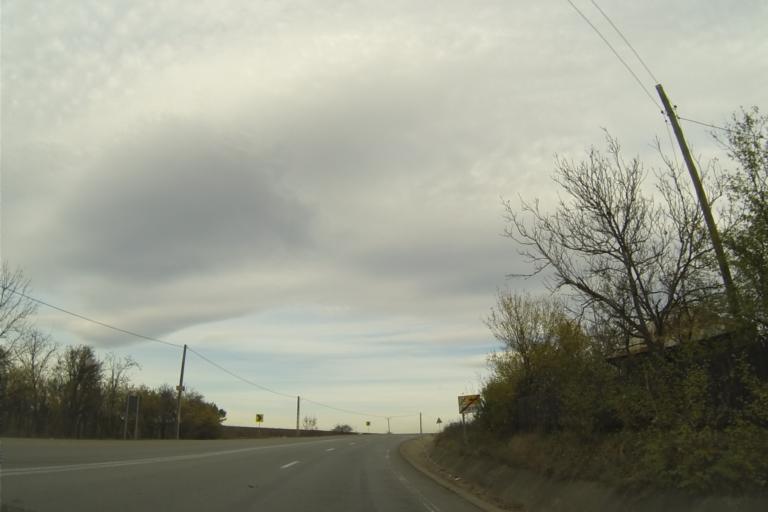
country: RO
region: Olt
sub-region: Comuna Scornicesti
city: Negreni
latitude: 44.5713
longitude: 24.5981
